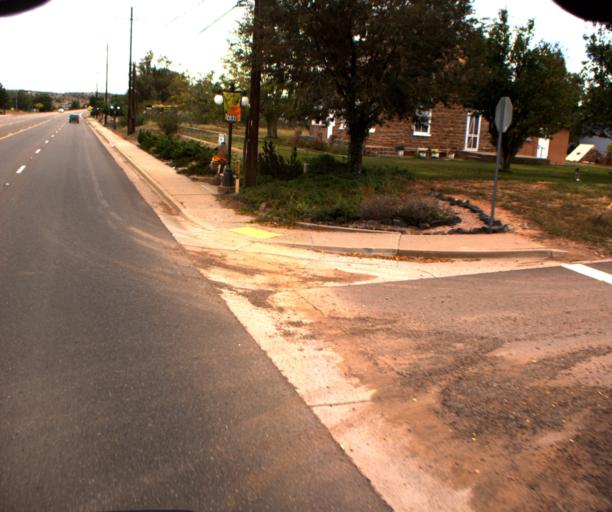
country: US
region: Arizona
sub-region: Navajo County
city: Taylor
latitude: 34.4610
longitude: -110.0912
